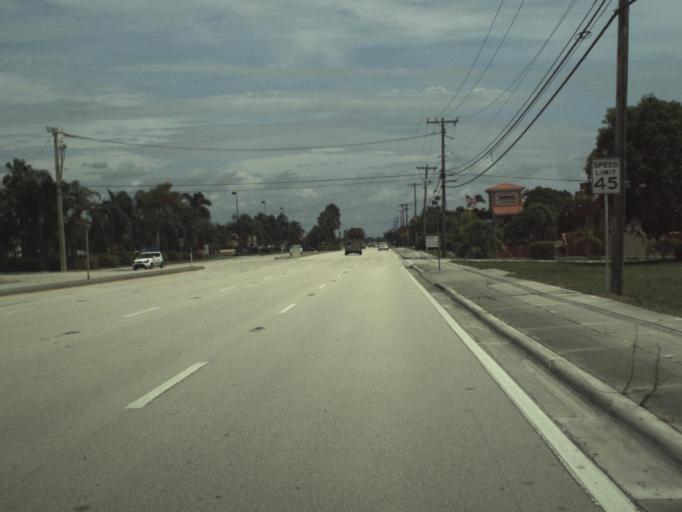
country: US
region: Florida
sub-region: Palm Beach County
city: Jupiter
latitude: 26.9649
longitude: -80.0853
